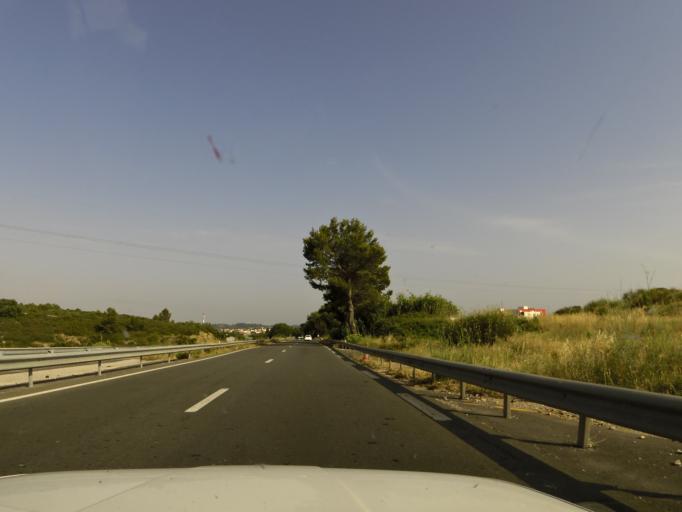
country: FR
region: Languedoc-Roussillon
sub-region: Departement de l'Herault
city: Grabels
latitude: 43.6255
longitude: 3.7856
